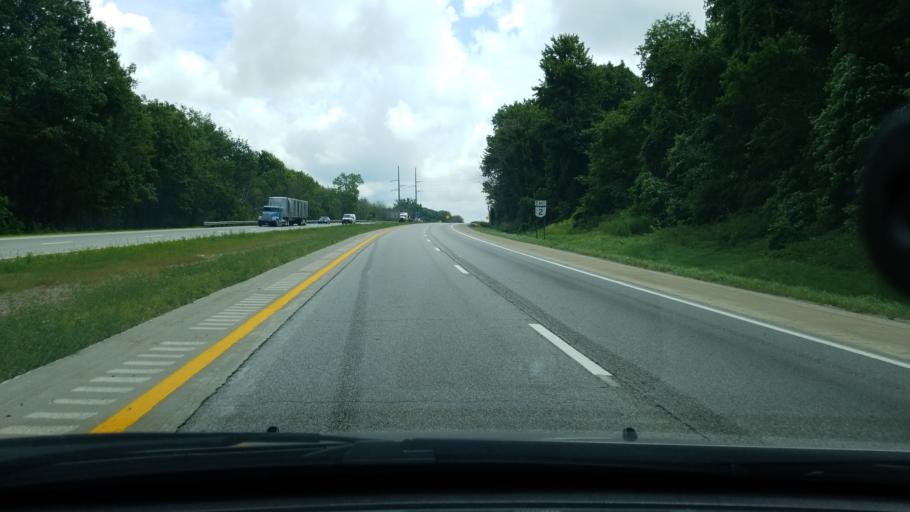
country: US
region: Ohio
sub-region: Lorain County
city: Lorain
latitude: 41.4100
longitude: -82.1574
